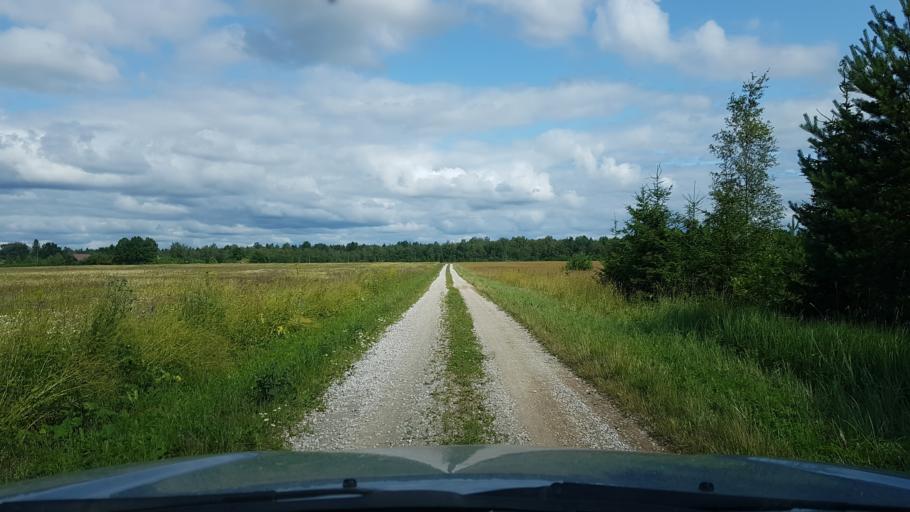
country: EE
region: Ida-Virumaa
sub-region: Narva-Joesuu linn
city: Narva-Joesuu
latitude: 59.3700
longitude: 27.9481
